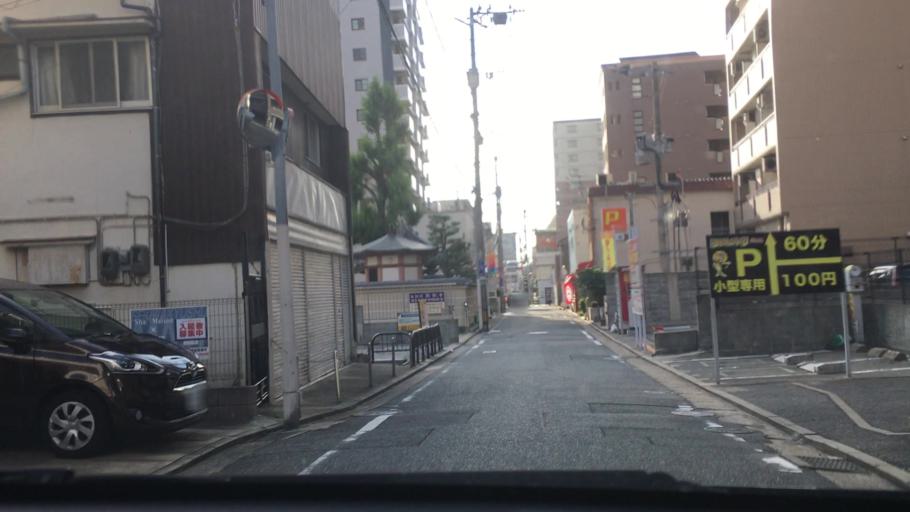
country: JP
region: Fukuoka
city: Fukuoka-shi
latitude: 33.6180
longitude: 130.4235
